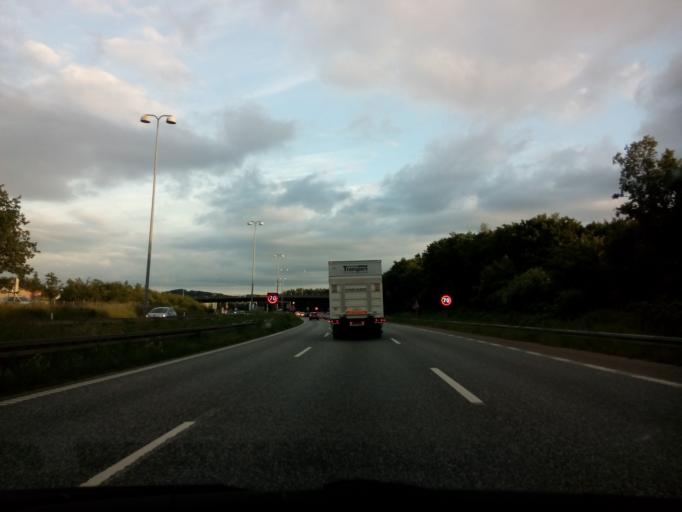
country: DK
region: North Denmark
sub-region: Alborg Kommune
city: Aalborg
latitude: 57.0643
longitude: 9.9488
